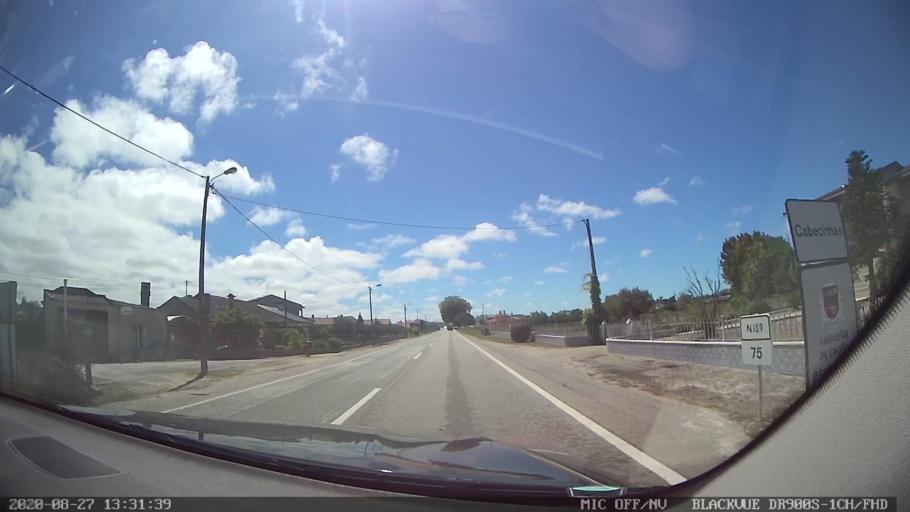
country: PT
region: Aveiro
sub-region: Vagos
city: Vagos
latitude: 40.4946
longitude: -8.6844
